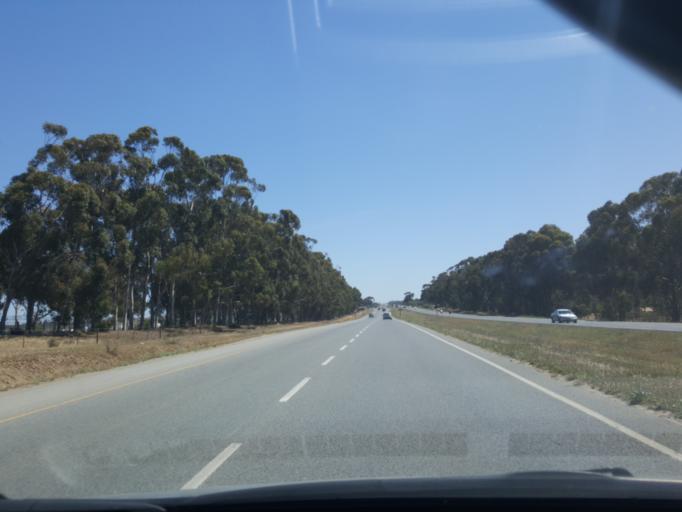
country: ZA
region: Western Cape
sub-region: City of Cape Town
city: Sunset Beach
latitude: -33.7740
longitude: 18.5483
